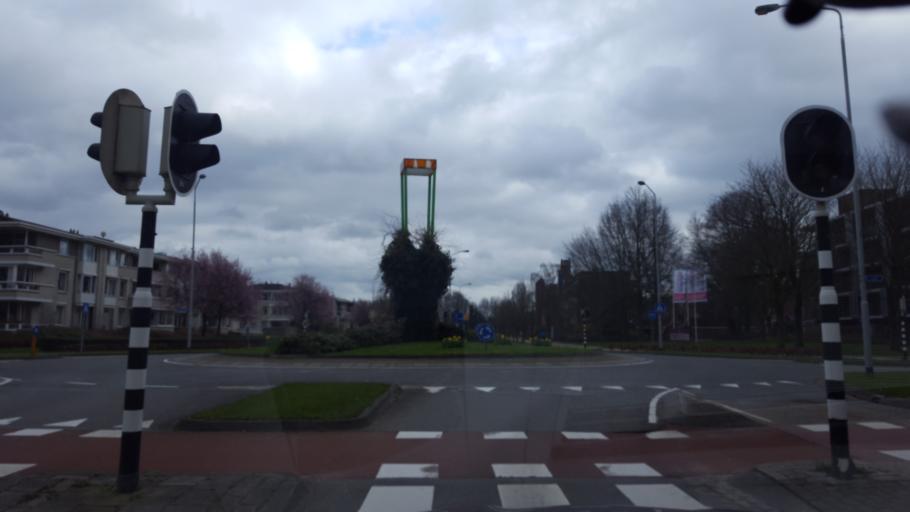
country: NL
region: North Brabant
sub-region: Gemeente Veldhoven
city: Veldhoven
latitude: 51.4214
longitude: 5.4081
